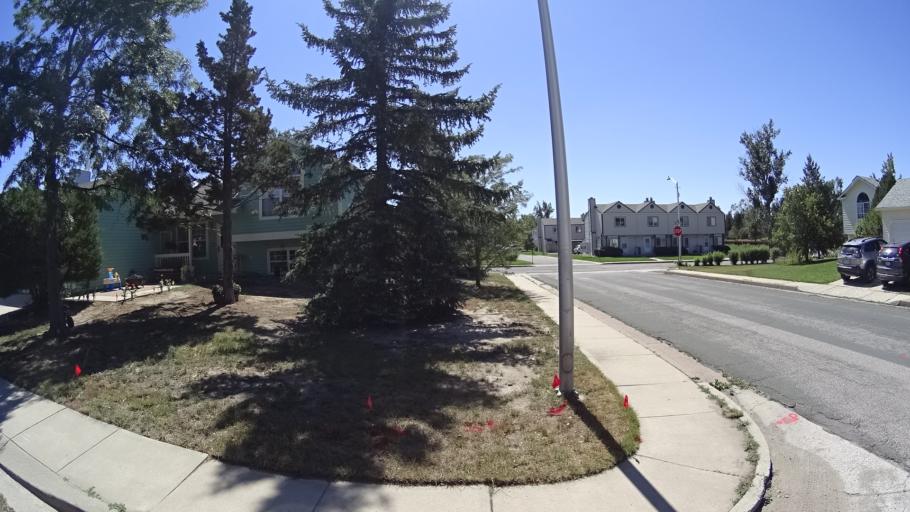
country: US
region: Colorado
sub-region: El Paso County
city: Black Forest
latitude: 38.9442
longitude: -104.7629
